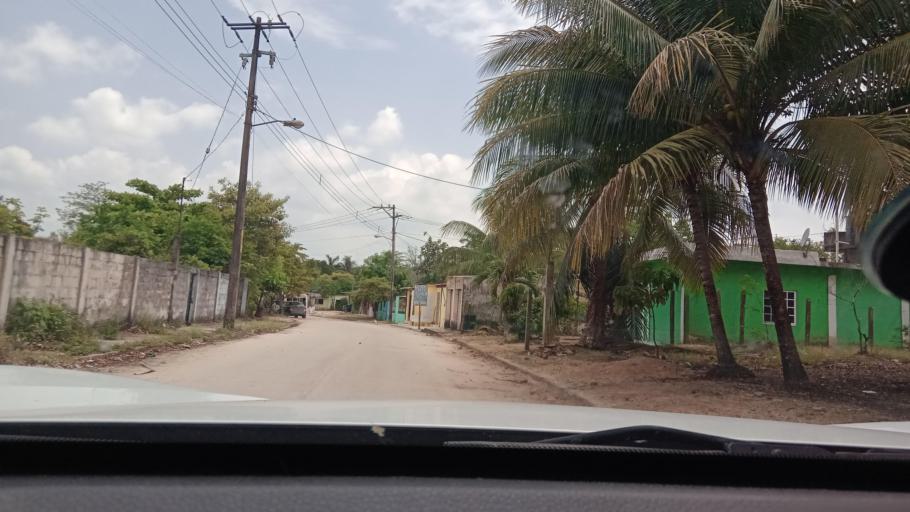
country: MX
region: Veracruz
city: Las Choapas
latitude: 17.8878
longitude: -94.1027
